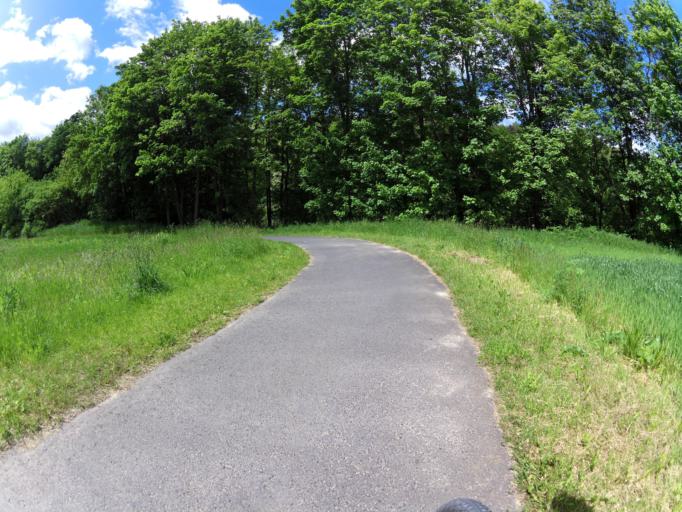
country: DE
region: Thuringia
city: Mihla
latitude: 51.0867
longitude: 10.3215
